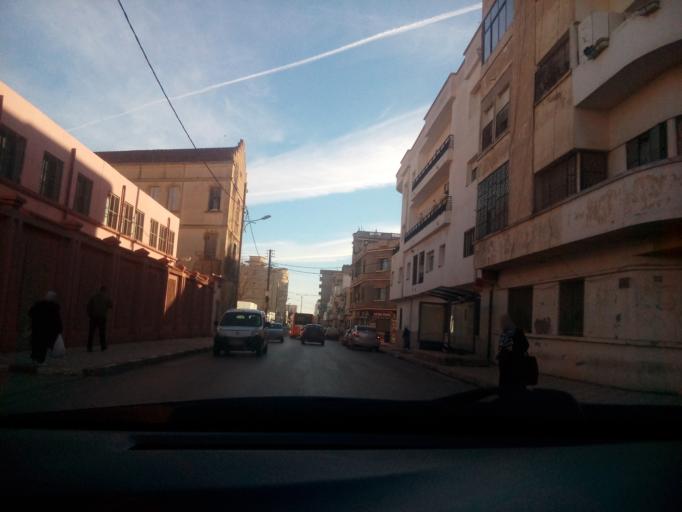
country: DZ
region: Oran
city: Oran
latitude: 35.6872
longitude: -0.6586
